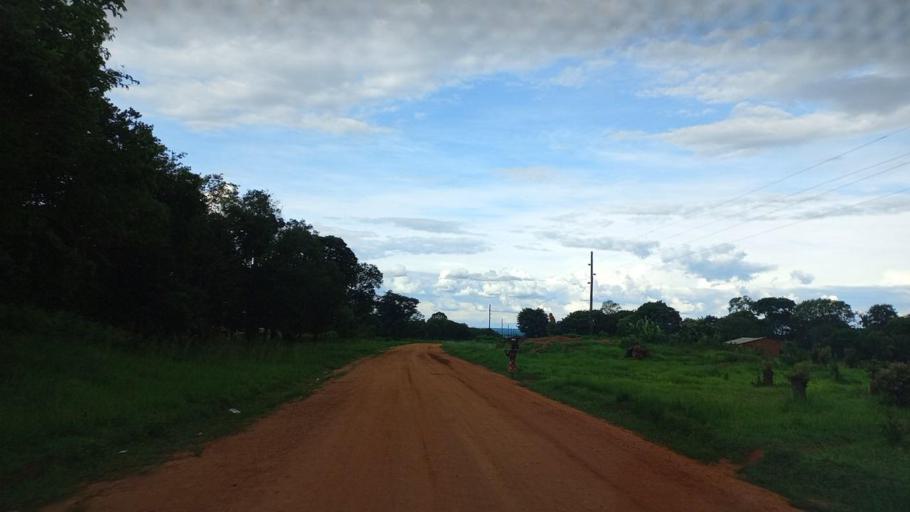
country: ZM
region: North-Western
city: Mwinilunga
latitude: -11.7695
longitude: 24.4086
